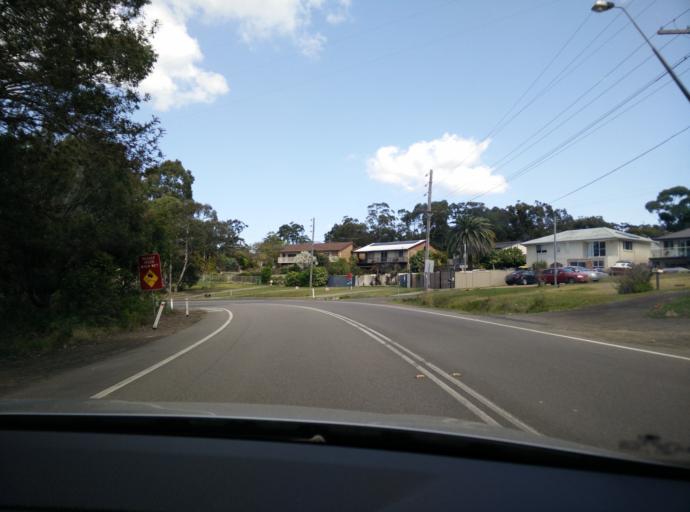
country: AU
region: New South Wales
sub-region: Gosford Shire
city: Blackwall
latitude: -33.4924
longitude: 151.2990
